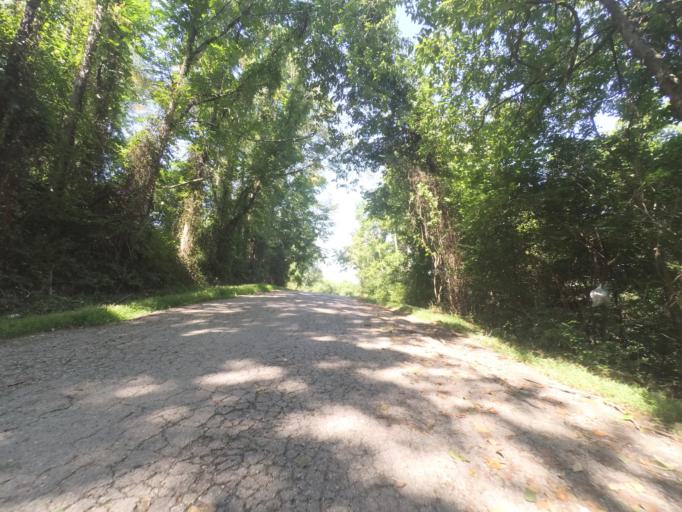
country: US
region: West Virginia
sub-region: Cabell County
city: Huntington
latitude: 38.4366
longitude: -82.4347
